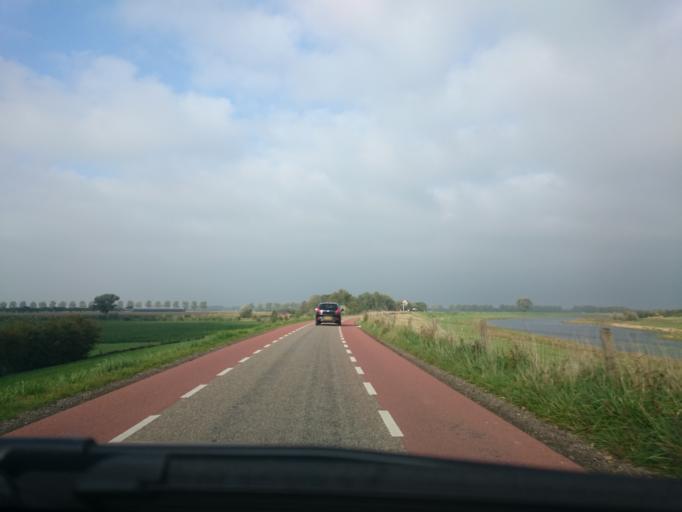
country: NL
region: North Brabant
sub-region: Gemeente Landerd
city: Reek
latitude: 51.7589
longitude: 5.6861
